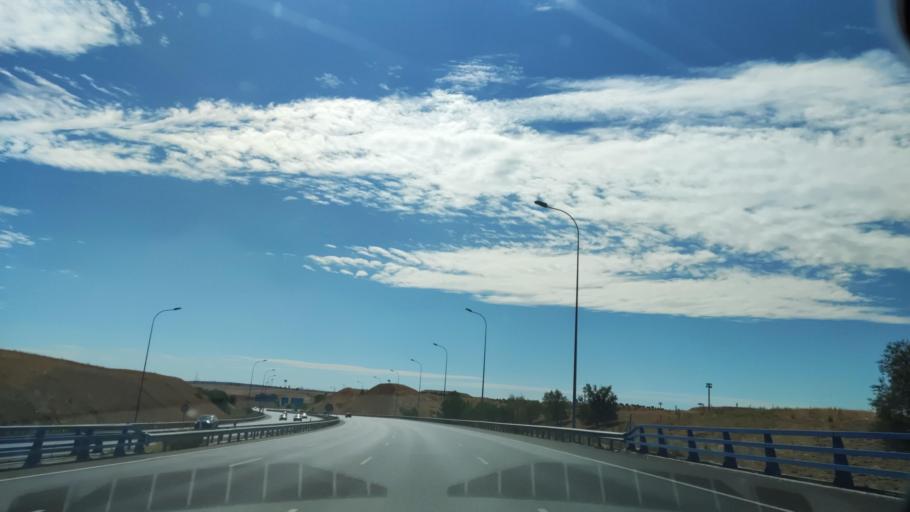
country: ES
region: Madrid
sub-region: Provincia de Madrid
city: Puente de Vallecas
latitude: 40.3682
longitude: -3.6493
